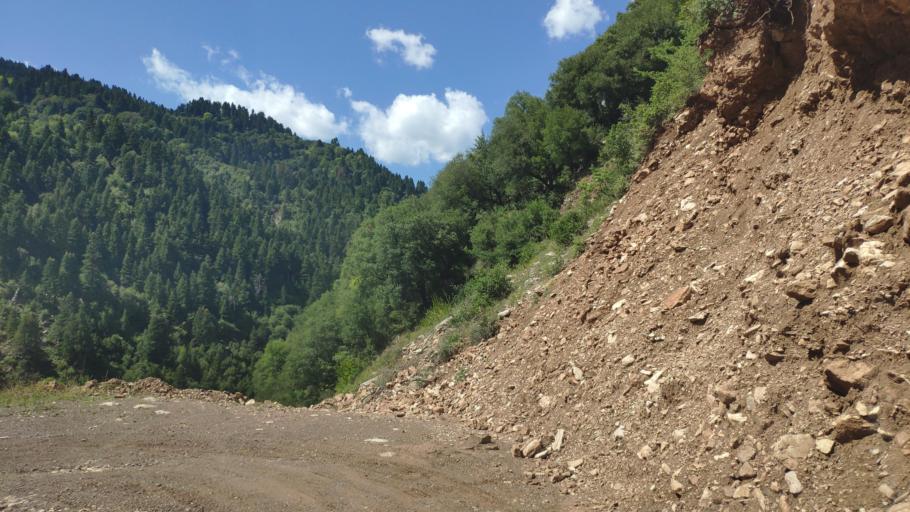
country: GR
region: Central Greece
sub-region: Nomos Evrytanias
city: Kerasochori
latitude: 39.1255
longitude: 21.6528
